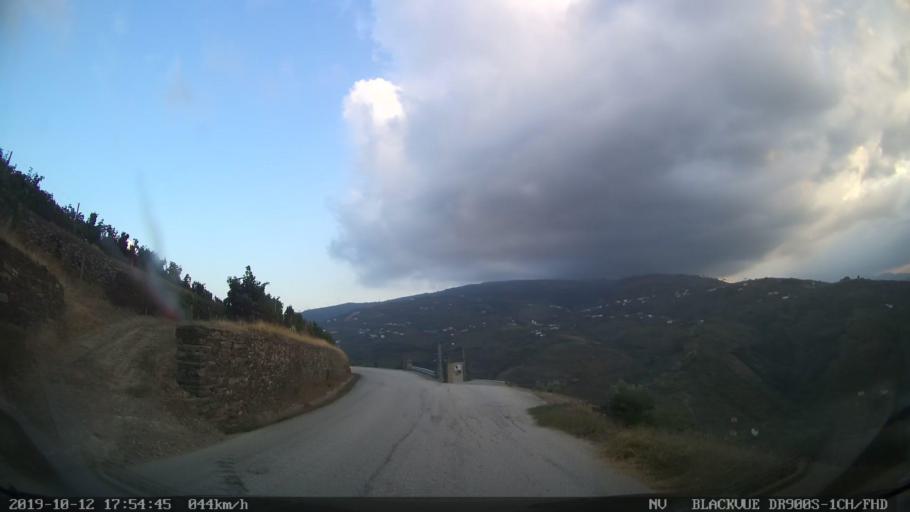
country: PT
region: Vila Real
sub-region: Mesao Frio
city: Mesao Frio
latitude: 41.1624
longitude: -7.8549
